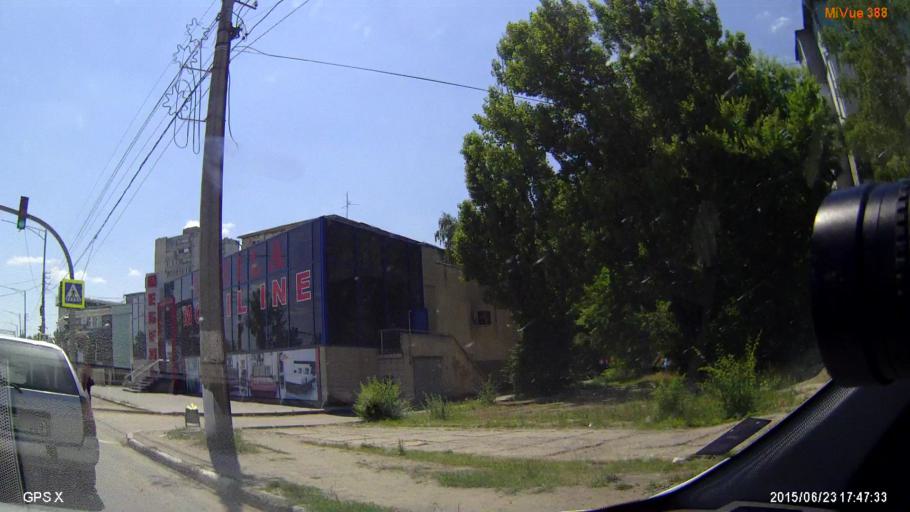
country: MD
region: Balti
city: Balti
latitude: 47.7661
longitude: 27.9415
